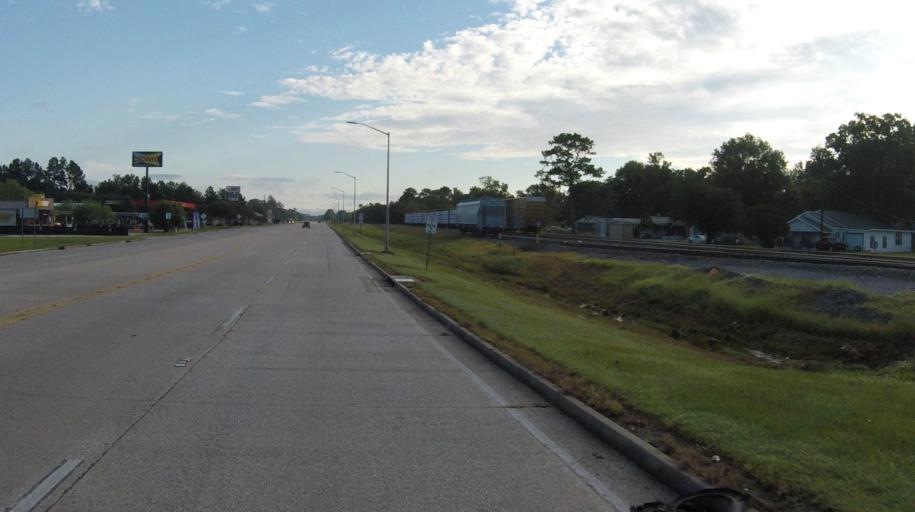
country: US
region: Louisiana
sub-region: Allen Parish
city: Kinder
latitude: 30.4933
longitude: -92.8444
